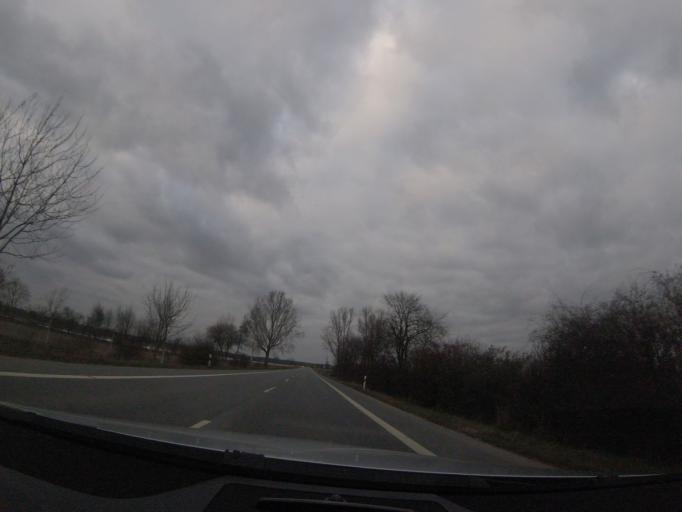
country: DE
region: Hesse
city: Weiterstadt
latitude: 49.9339
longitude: 8.5935
